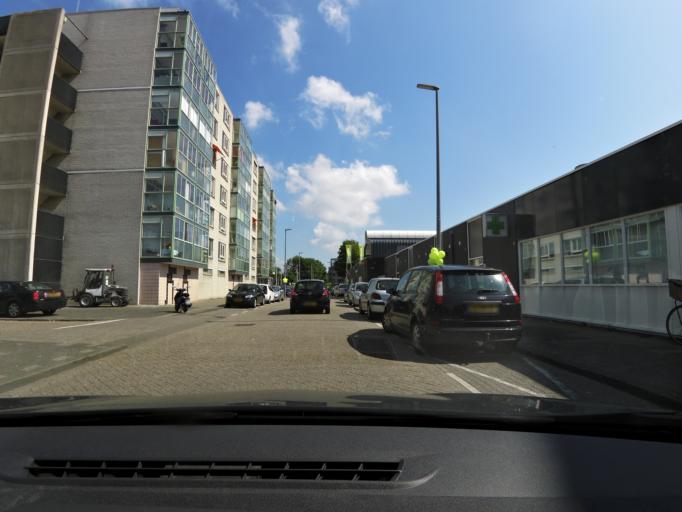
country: NL
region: South Holland
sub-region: Gemeente Rotterdam
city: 's-Gravenland
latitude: 51.9137
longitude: 4.5204
